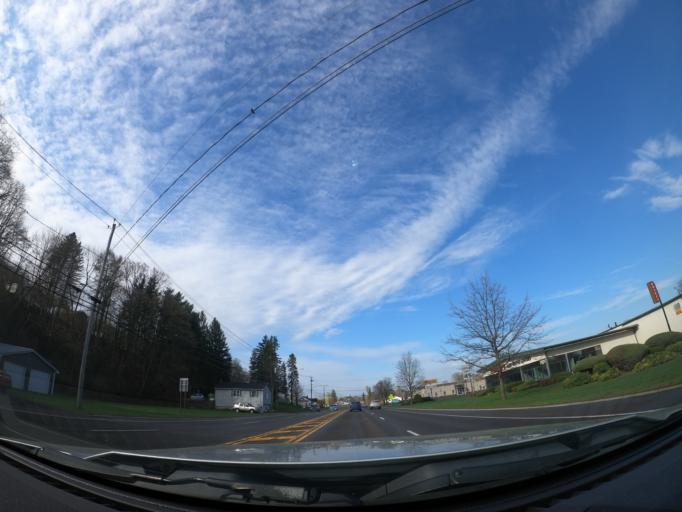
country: US
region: New York
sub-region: Cortland County
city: Munsons Corners
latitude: 42.5802
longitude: -76.2088
